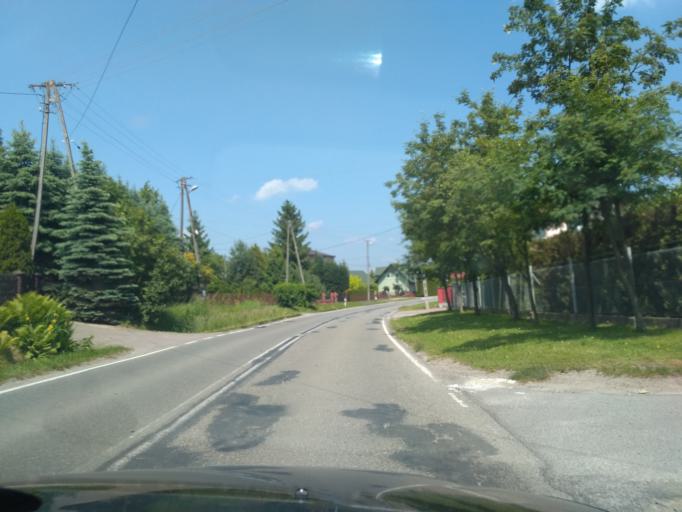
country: PL
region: Subcarpathian Voivodeship
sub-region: Powiat lancucki
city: Albigowa
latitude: 50.0210
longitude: 22.2243
